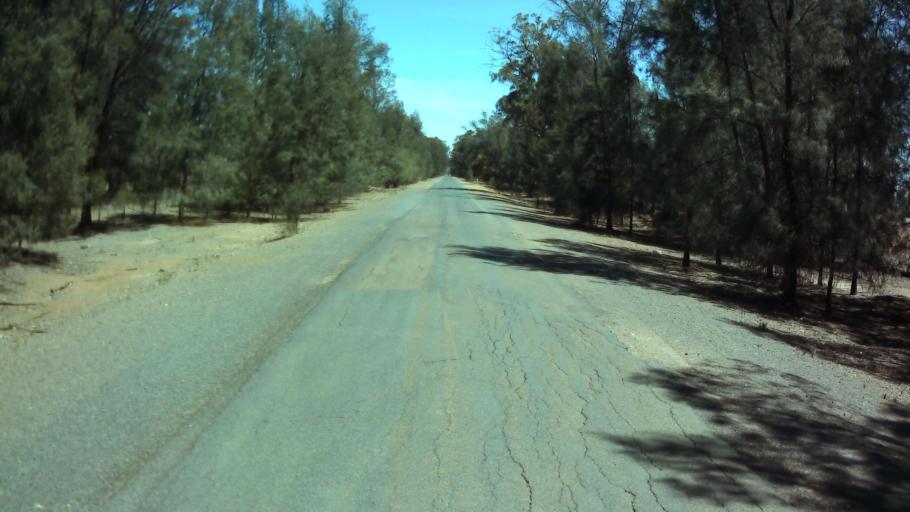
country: AU
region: New South Wales
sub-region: Weddin
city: Grenfell
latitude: -33.8775
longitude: 147.6908
